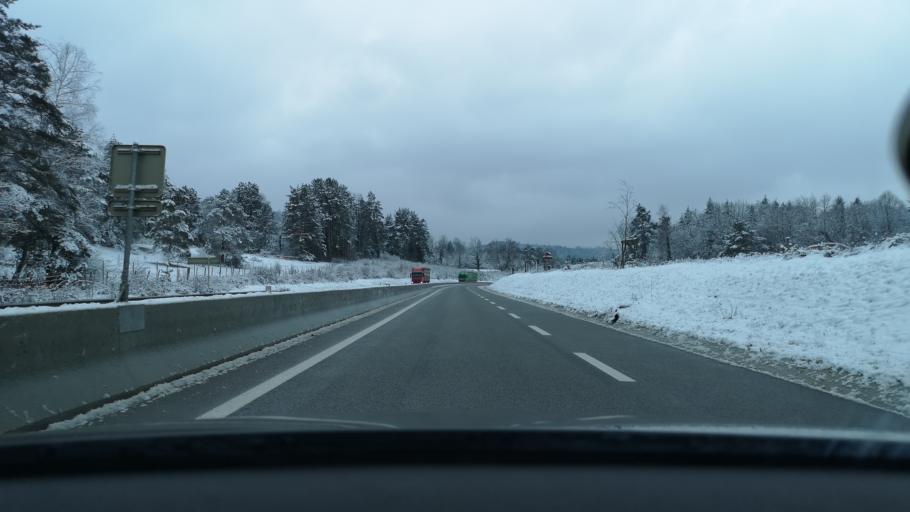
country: FR
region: Rhone-Alpes
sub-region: Departement de l'Ain
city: Dortan
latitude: 46.3106
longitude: 5.6684
